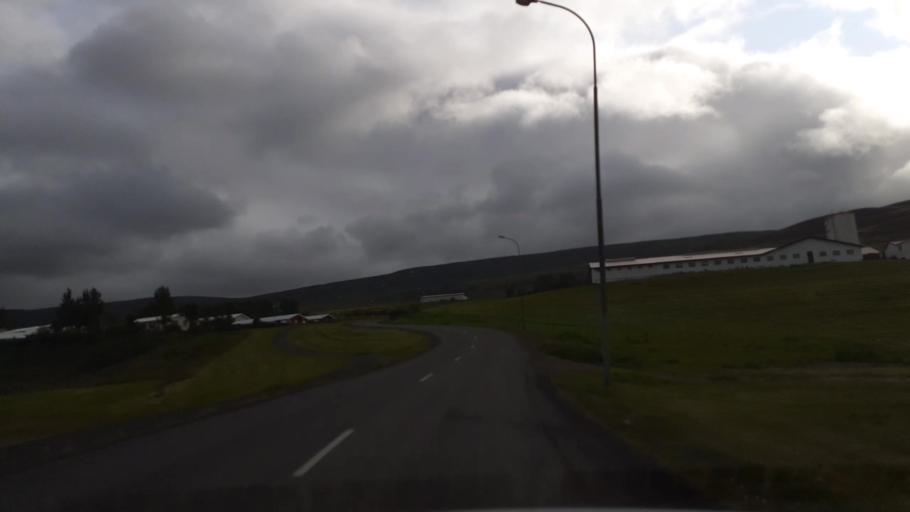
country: IS
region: Northeast
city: Akureyri
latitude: 65.7447
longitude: -18.0875
